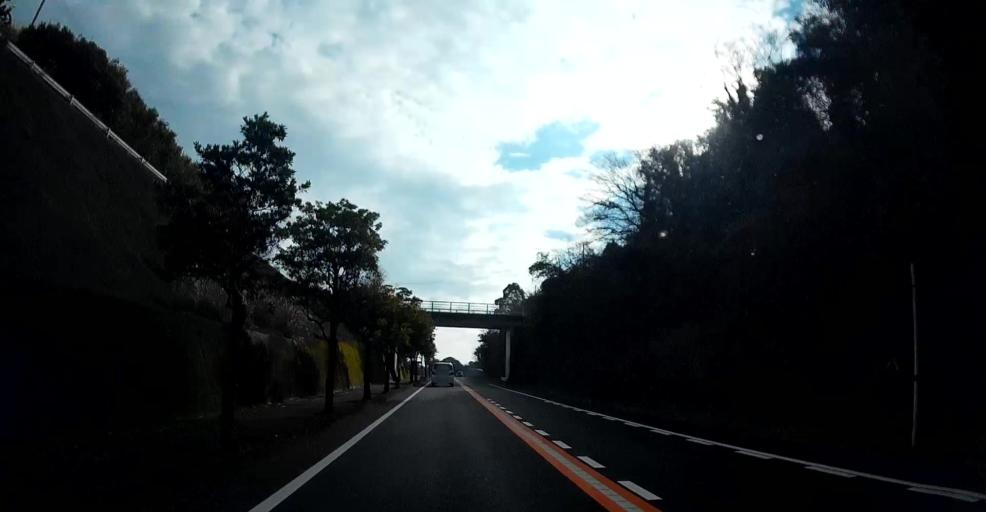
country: JP
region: Kumamoto
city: Yatsushiro
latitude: 32.5991
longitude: 130.4358
